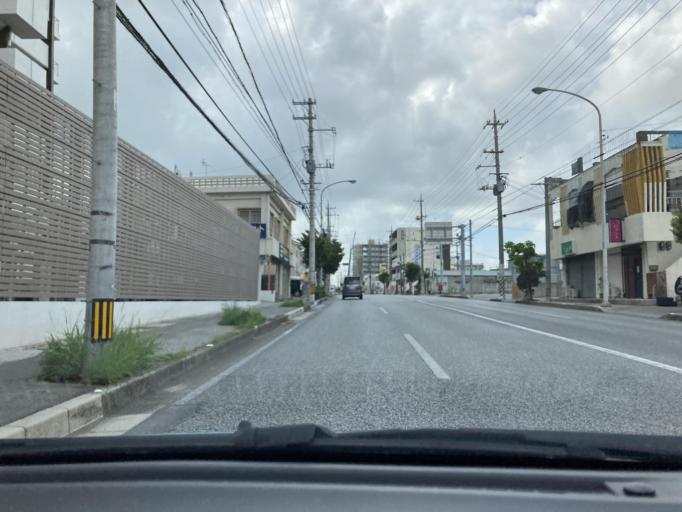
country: JP
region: Okinawa
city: Okinawa
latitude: 26.3438
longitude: 127.8202
